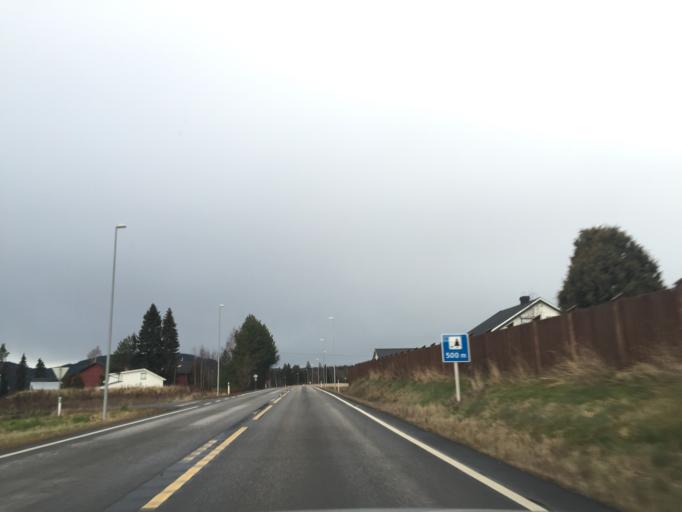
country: NO
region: Hedmark
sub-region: Asnes
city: Flisa
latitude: 60.6063
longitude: 12.0455
